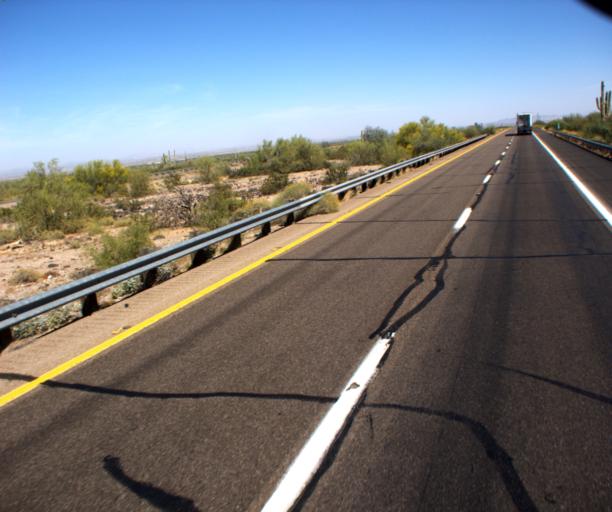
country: US
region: Arizona
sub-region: Pinal County
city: Maricopa
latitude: 32.8315
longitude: -112.0608
